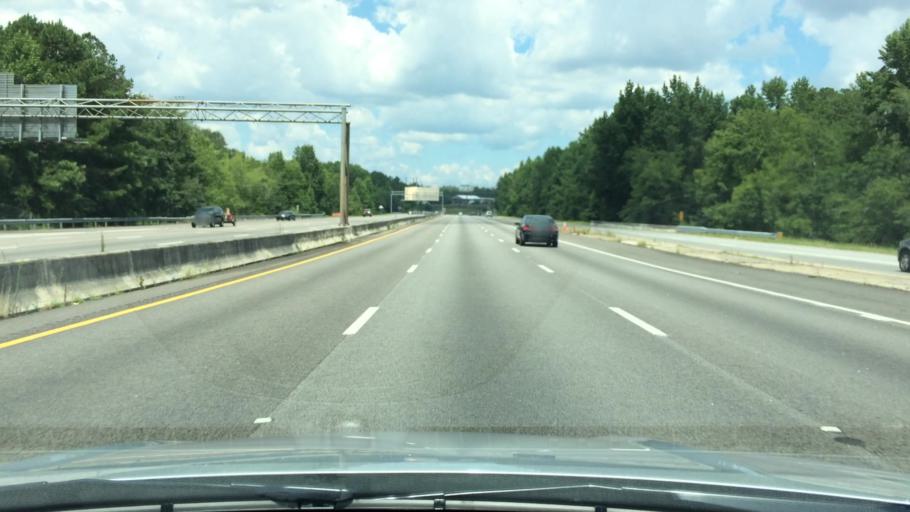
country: US
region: South Carolina
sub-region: Lexington County
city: Cayce
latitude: 33.9345
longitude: -81.0796
